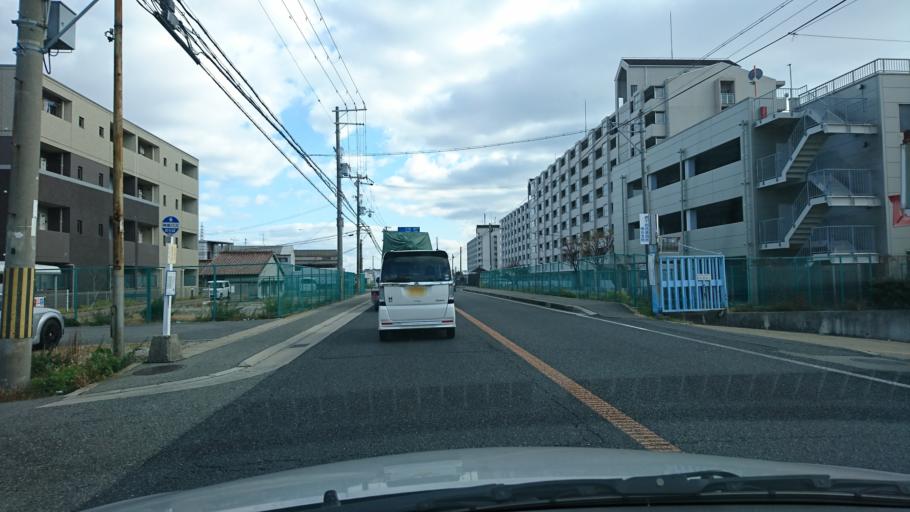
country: JP
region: Hyogo
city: Akashi
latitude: 34.6607
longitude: 134.9691
